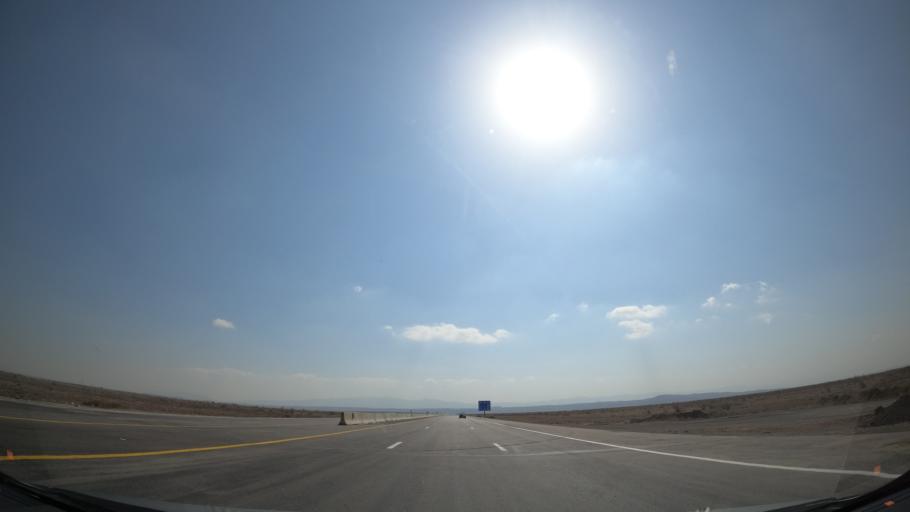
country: IR
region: Alborz
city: Nazarabad
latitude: 35.8624
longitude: 50.4795
